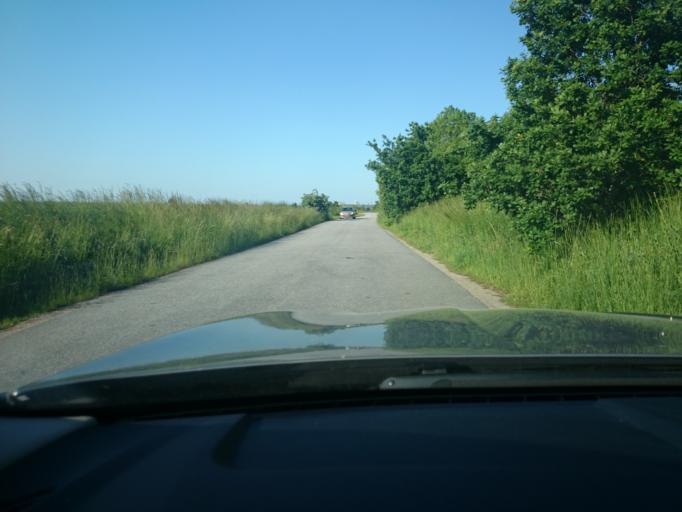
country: SE
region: Skane
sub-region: Staffanstorps Kommun
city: Hjaerup
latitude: 55.6756
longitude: 13.1387
